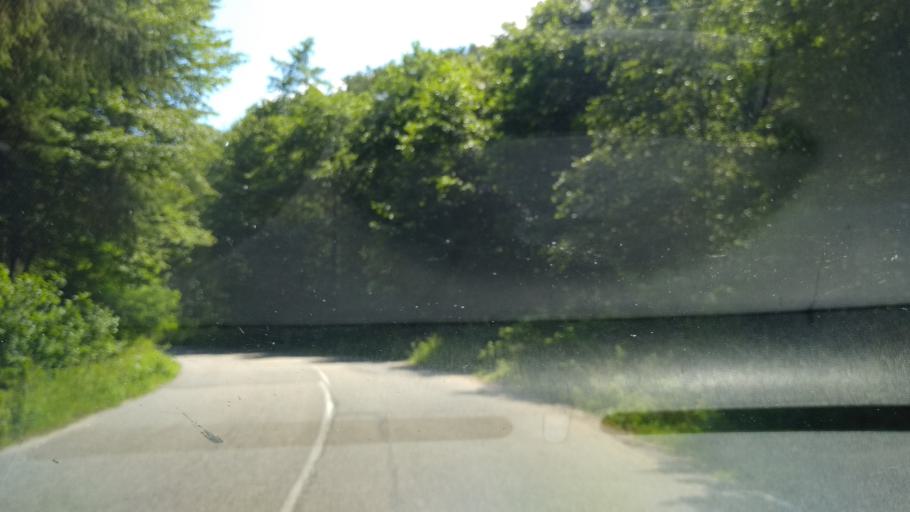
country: RO
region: Hunedoara
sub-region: Comuna Orastioara de Sus
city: Orastioara de Sus
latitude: 45.6456
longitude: 23.1935
